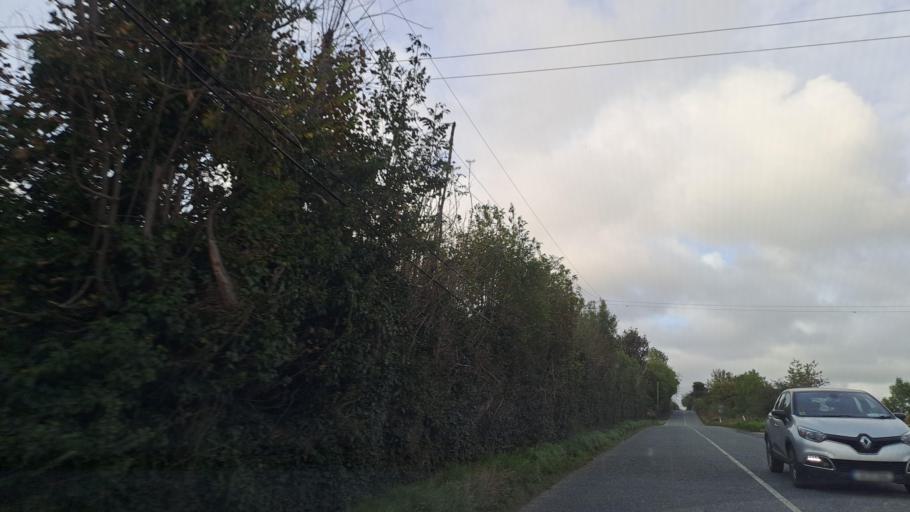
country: IE
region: Ulster
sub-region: An Cabhan
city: Kingscourt
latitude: 53.8871
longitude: -6.8023
